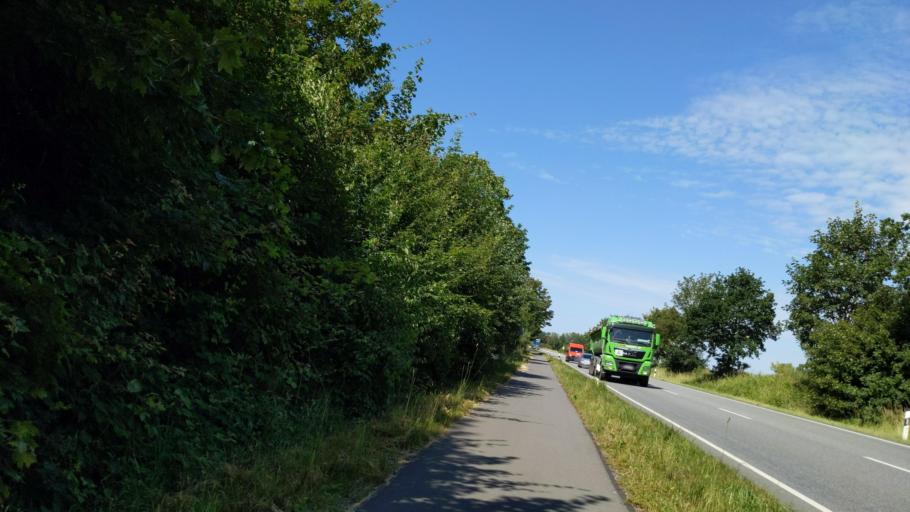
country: DE
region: Schleswig-Holstein
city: Bosdorf
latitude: 54.1331
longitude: 10.5267
